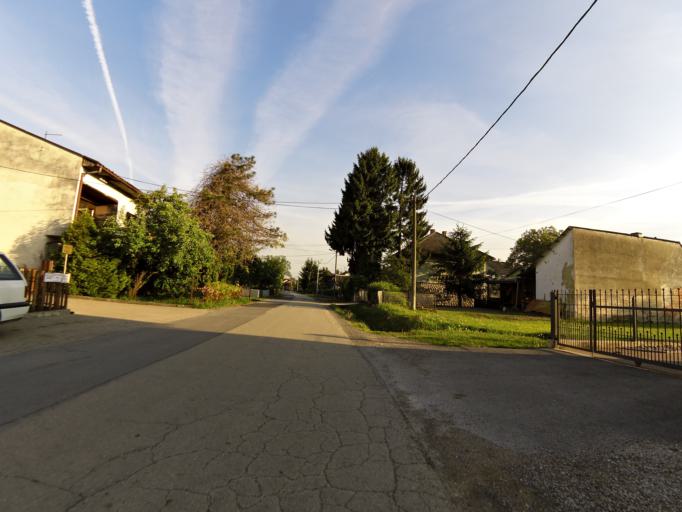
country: HR
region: Karlovacka
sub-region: Grad Karlovac
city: Karlovac
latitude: 45.5067
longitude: 15.5311
